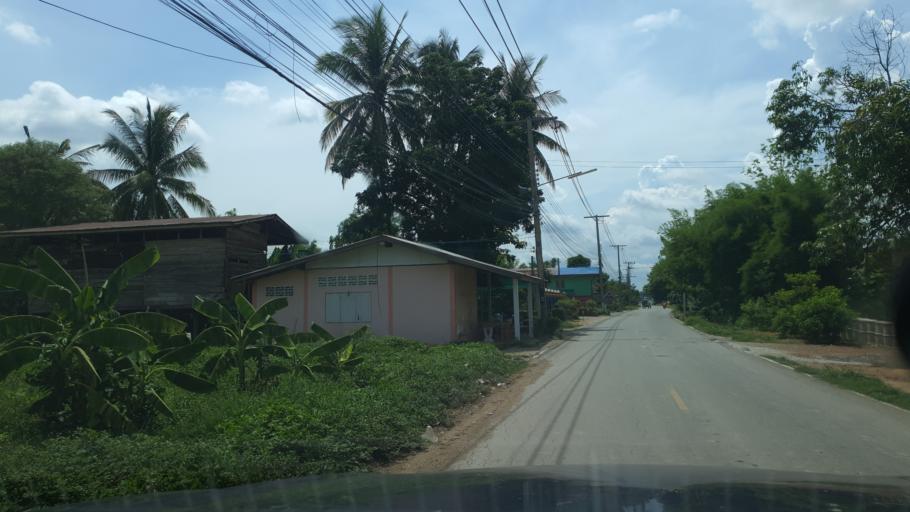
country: TH
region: Sukhothai
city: Sukhothai
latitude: 16.9965
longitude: 99.8554
